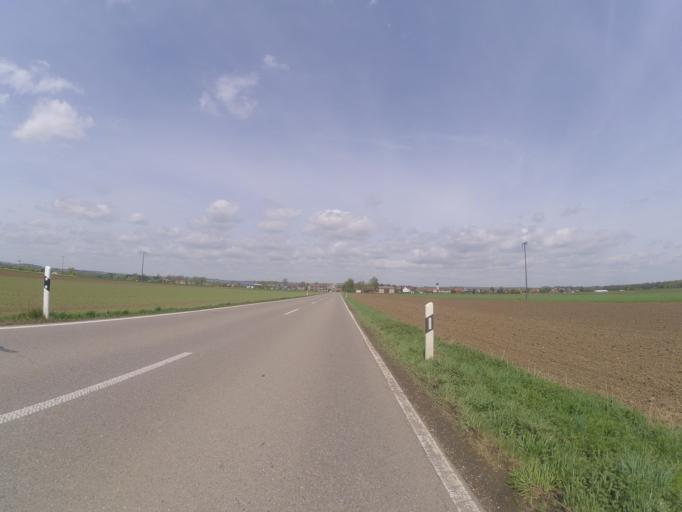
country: DE
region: Baden-Wuerttemberg
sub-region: Tuebingen Region
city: Ersingen
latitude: 48.2852
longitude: 9.8552
